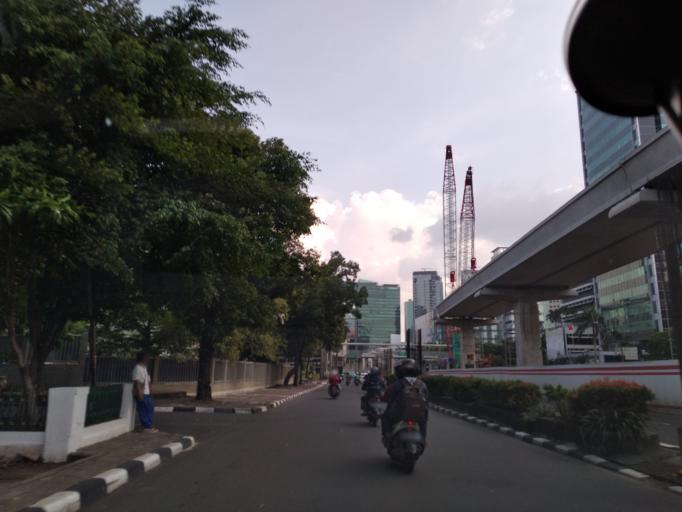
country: ID
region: Jakarta Raya
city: Jakarta
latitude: -6.2114
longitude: 106.8307
